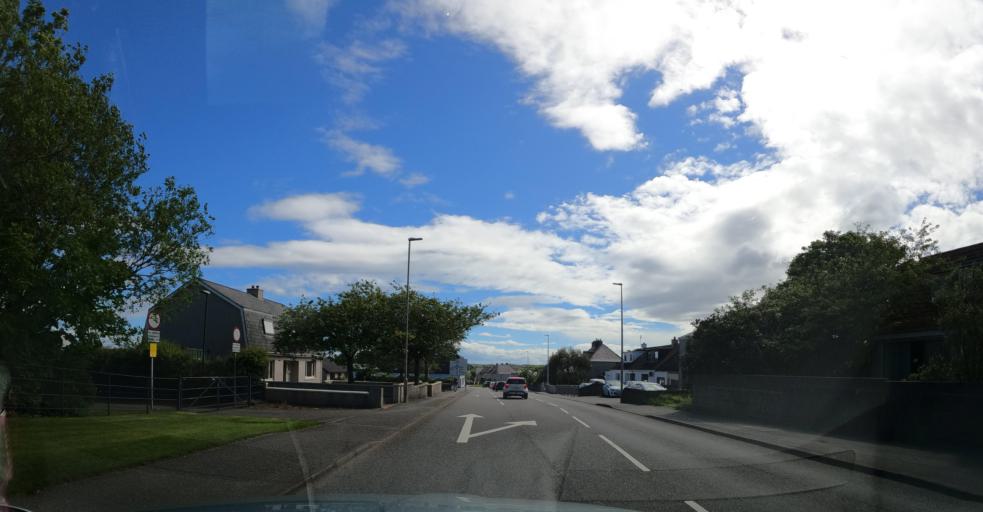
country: GB
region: Scotland
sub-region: Eilean Siar
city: Isle of Lewis
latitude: 58.2205
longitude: -6.3861
